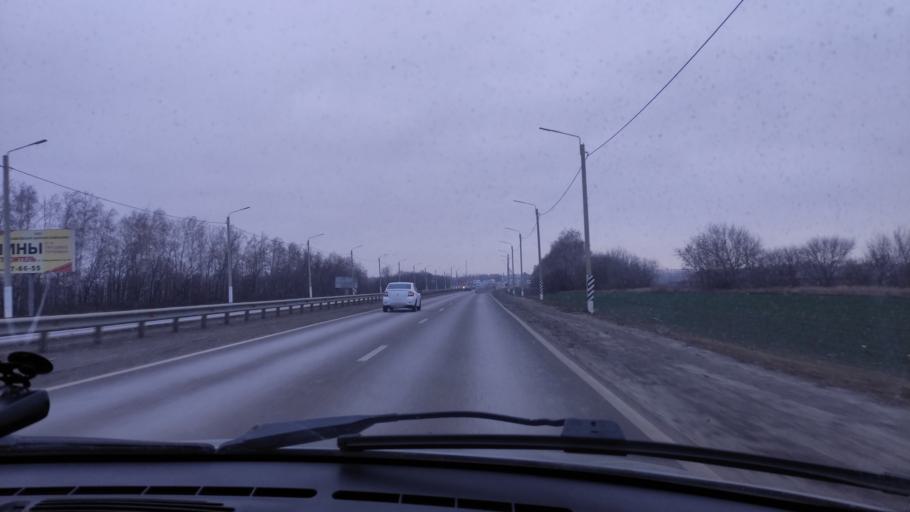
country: RU
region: Tambov
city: Komsomolets
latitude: 52.7263
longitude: 41.3426
